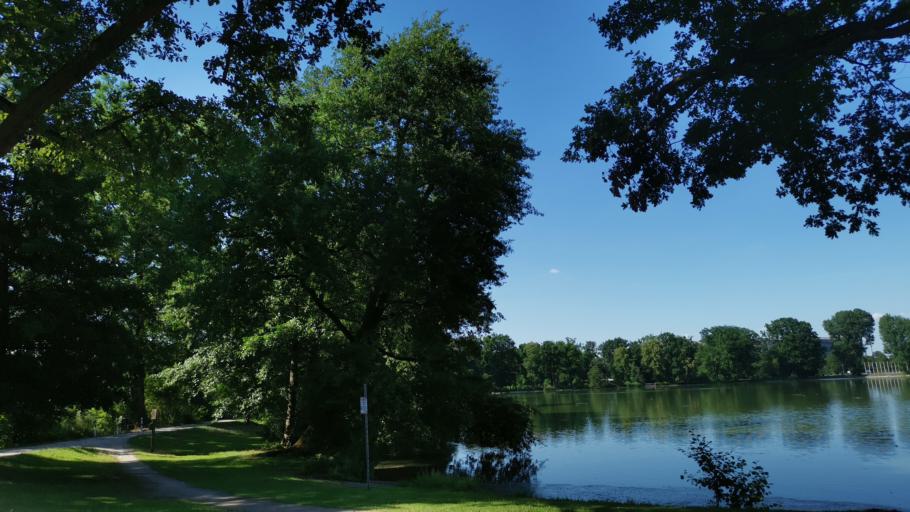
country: DE
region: Bavaria
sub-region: Regierungsbezirk Mittelfranken
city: Nuernberg
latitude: 49.4245
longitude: 11.1088
